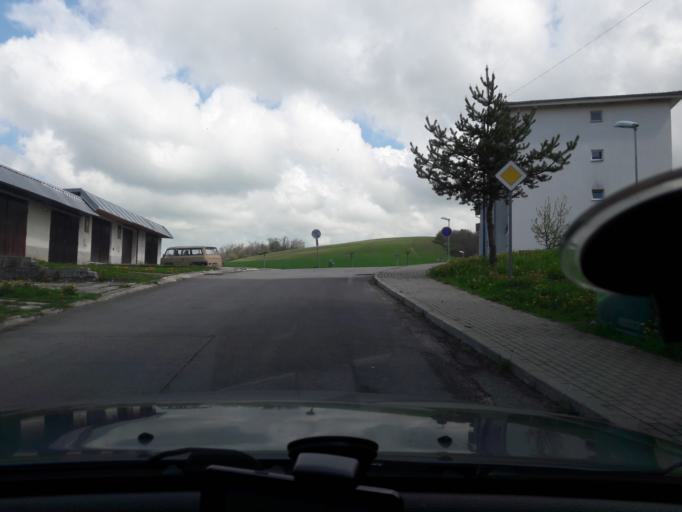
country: SK
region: Banskobystricky
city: Krupina
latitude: 48.4279
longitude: 19.1490
